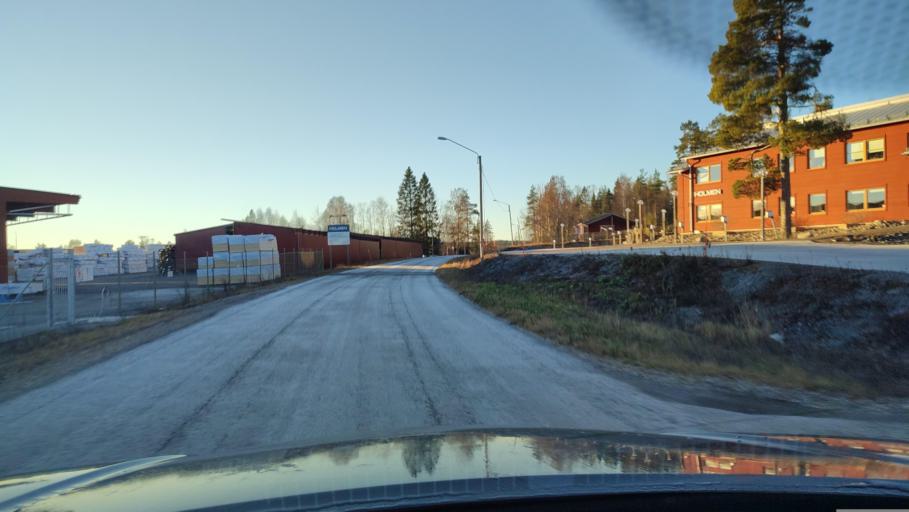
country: SE
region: Vaesterbotten
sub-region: Skelleftea Kommun
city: Viken
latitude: 64.7035
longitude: 20.9039
